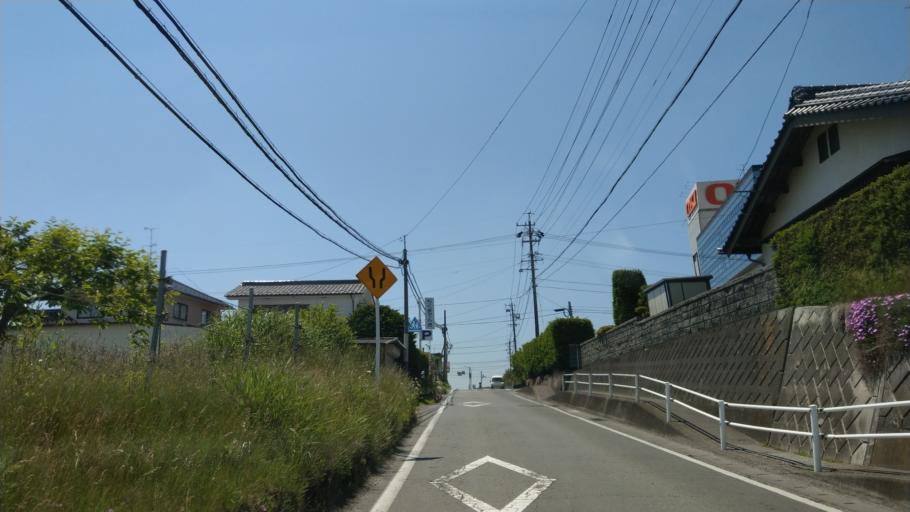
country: JP
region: Nagano
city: Komoro
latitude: 36.2919
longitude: 138.4400
